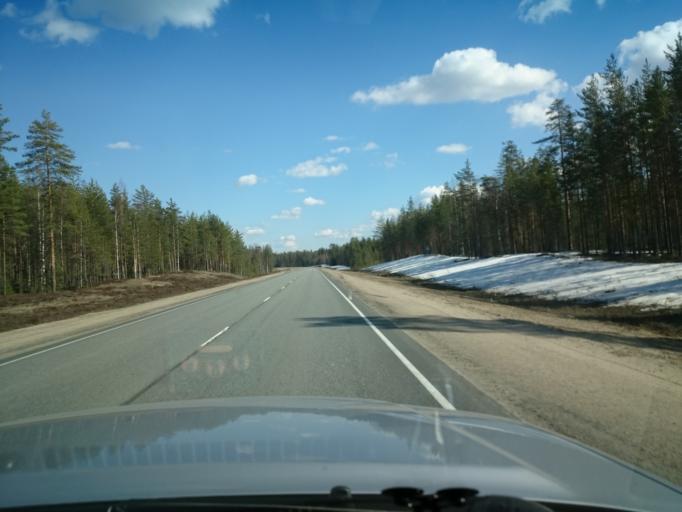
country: RU
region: Republic of Karelia
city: Pryazha
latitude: 61.4588
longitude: 33.3096
